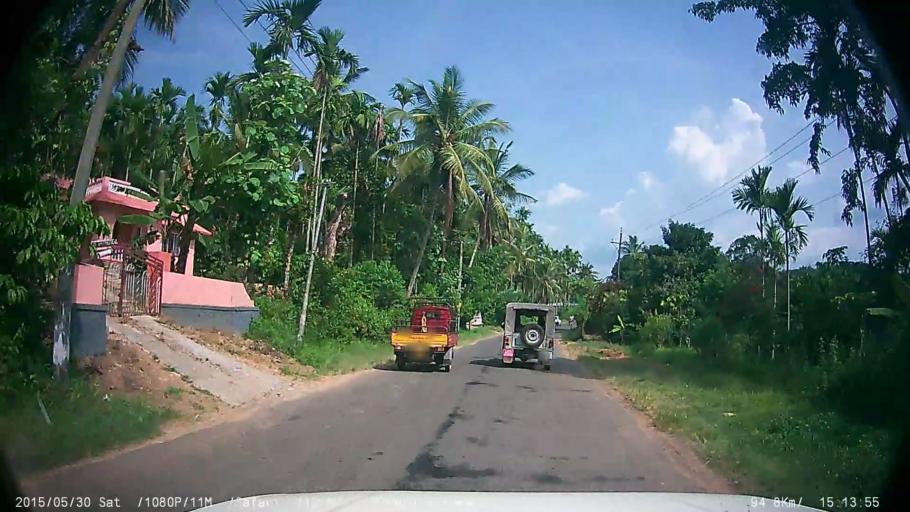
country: IN
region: Kerala
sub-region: Wayanad
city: Panamaram
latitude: 11.7889
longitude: 76.0450
